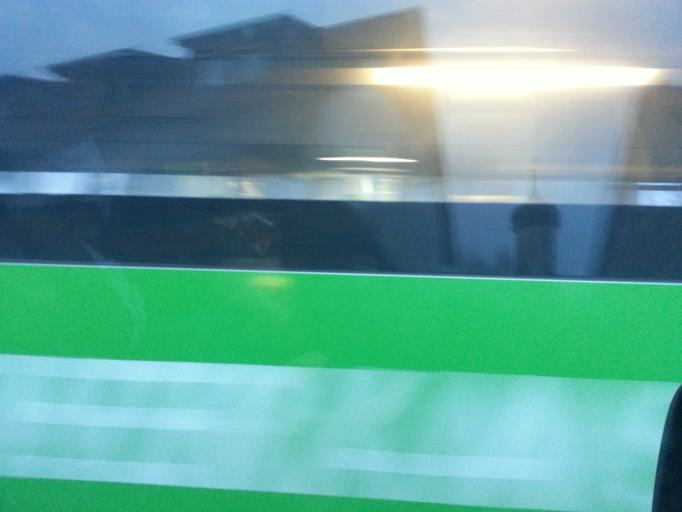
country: DE
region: Baden-Wuerttemberg
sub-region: Tuebingen Region
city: Markdorf
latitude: 47.6925
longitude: 9.4002
